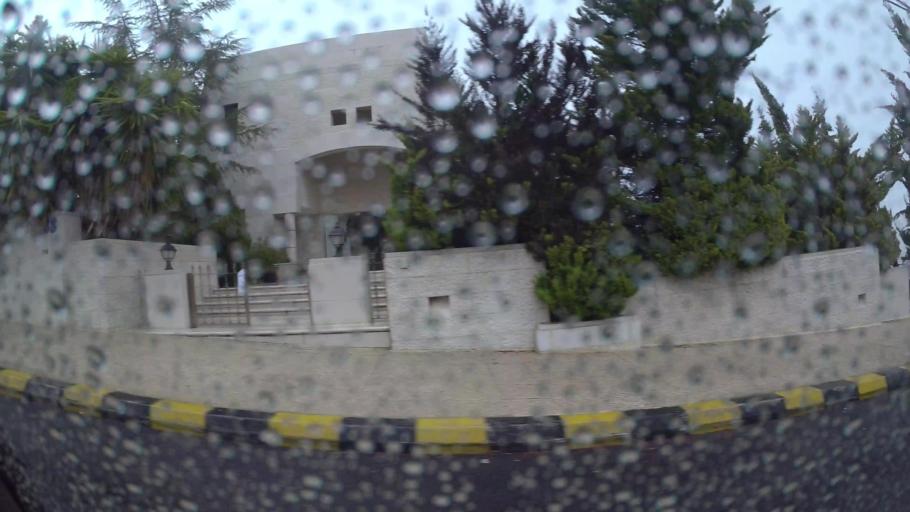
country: JO
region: Amman
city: Al Jubayhah
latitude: 32.0089
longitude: 35.8273
